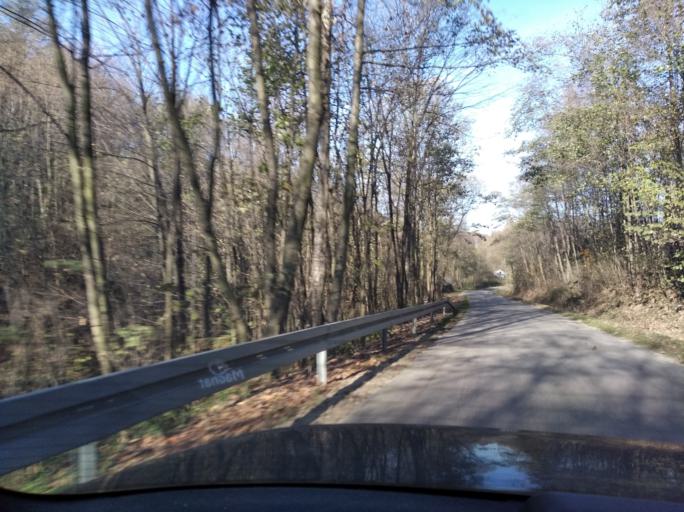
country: PL
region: Subcarpathian Voivodeship
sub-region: Powiat ropczycko-sedziszowski
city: Wielopole Skrzynskie
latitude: 49.9039
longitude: 21.5686
